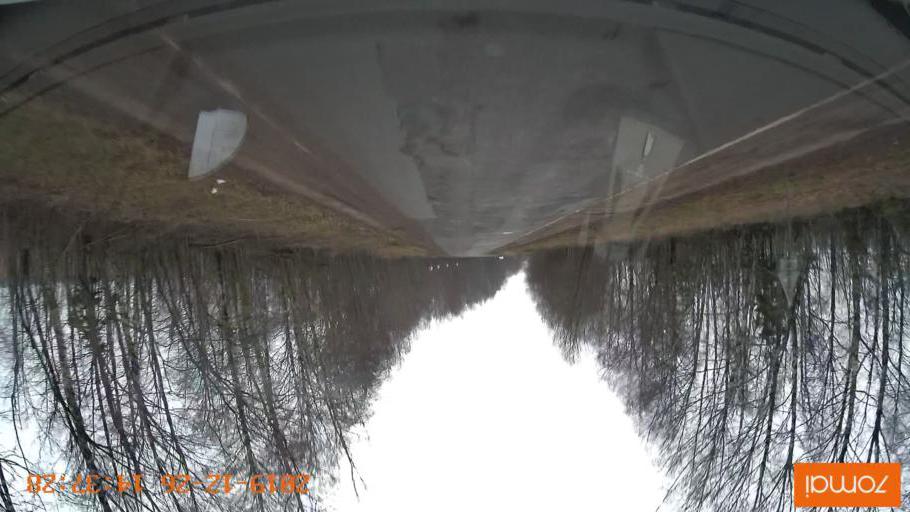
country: RU
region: Jaroslavl
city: Poshekhon'ye
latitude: 58.4021
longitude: 38.9722
